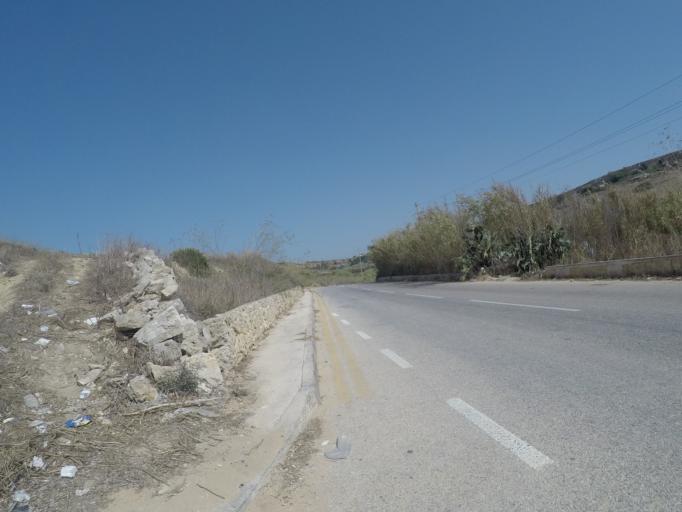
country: MT
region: L-Imgarr
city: Imgarr
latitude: 35.9200
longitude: 14.3477
